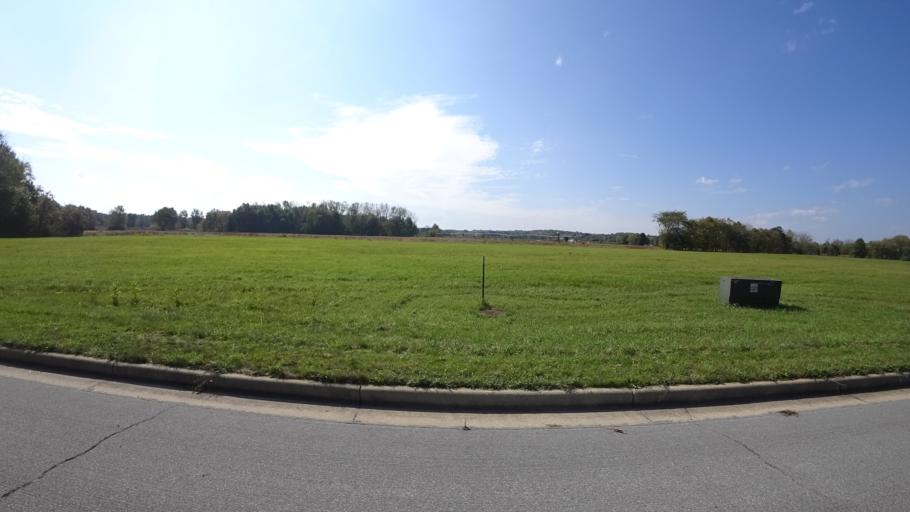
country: US
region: Michigan
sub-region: Saint Joseph County
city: Three Rivers
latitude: 41.9261
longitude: -85.6473
